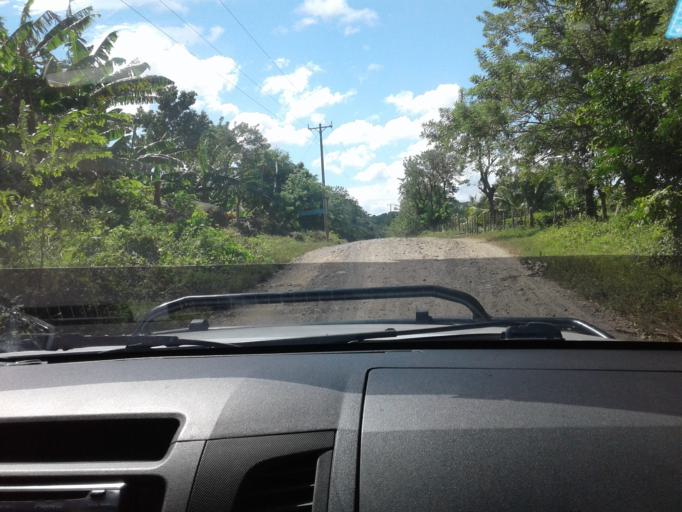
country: NI
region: Rivas
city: Altagracia
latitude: 11.4757
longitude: -85.5544
